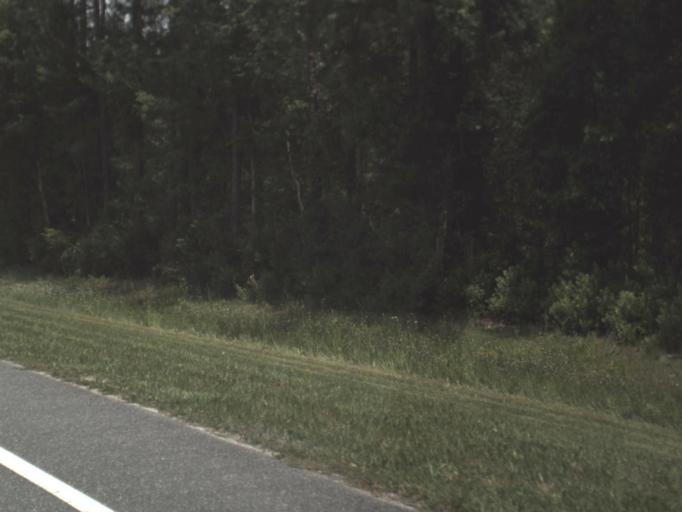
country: US
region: Florida
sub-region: Columbia County
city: Watertown
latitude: 30.1220
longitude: -82.5115
